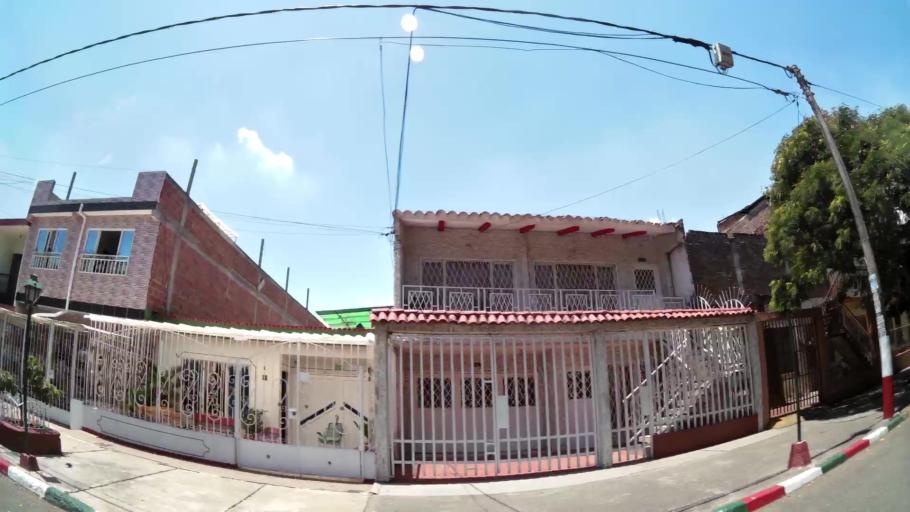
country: CO
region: Valle del Cauca
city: Cali
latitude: 3.4332
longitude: -76.5055
